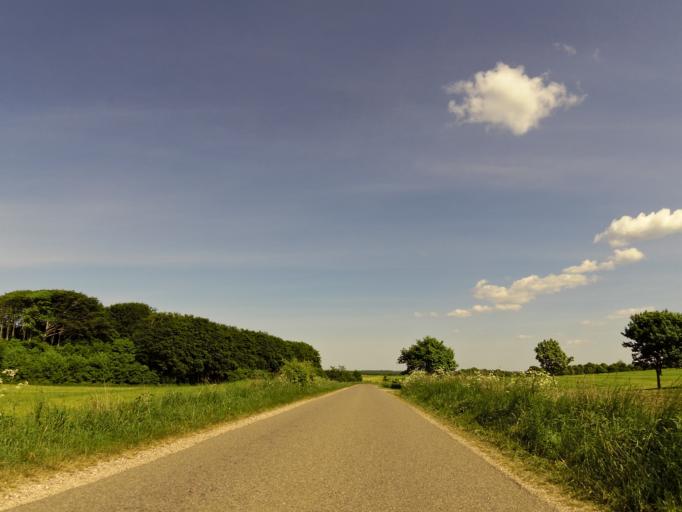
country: DK
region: Central Jutland
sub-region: Holstebro Kommune
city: Vinderup
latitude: 56.4367
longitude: 8.8753
